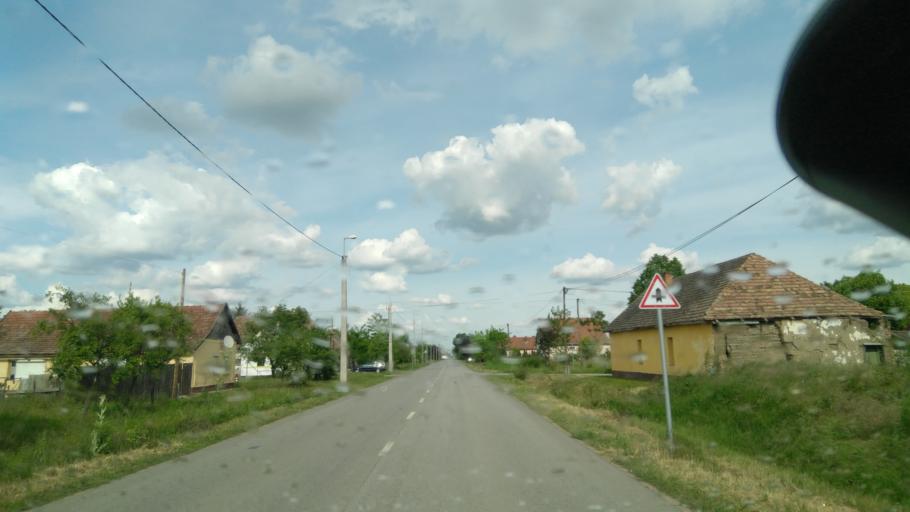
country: HU
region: Bekes
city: Battonya
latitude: 46.2918
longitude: 21.0076
